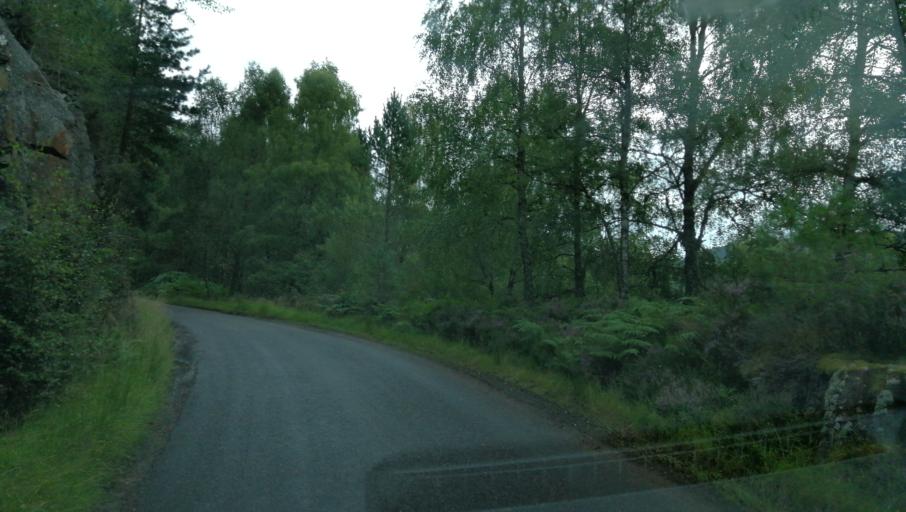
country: GB
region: Scotland
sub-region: Highland
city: Spean Bridge
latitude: 57.2991
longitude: -4.8986
